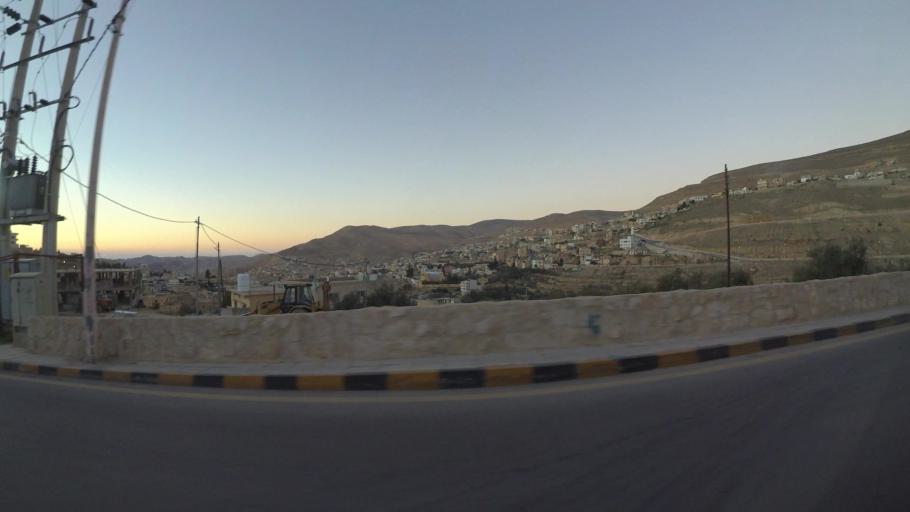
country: JO
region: Ma'an
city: Petra
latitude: 30.3118
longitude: 35.4806
